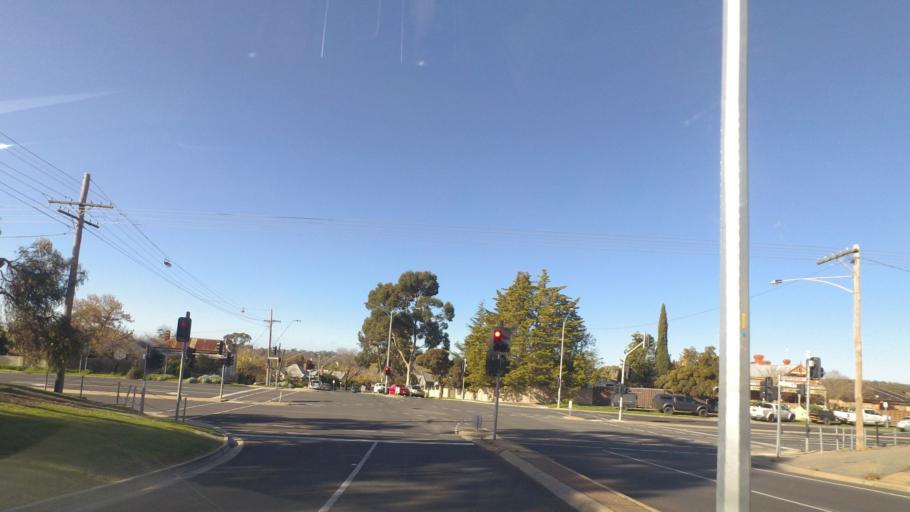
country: AU
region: Victoria
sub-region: Greater Bendigo
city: Quarry Hill
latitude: -36.7693
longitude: 144.2858
